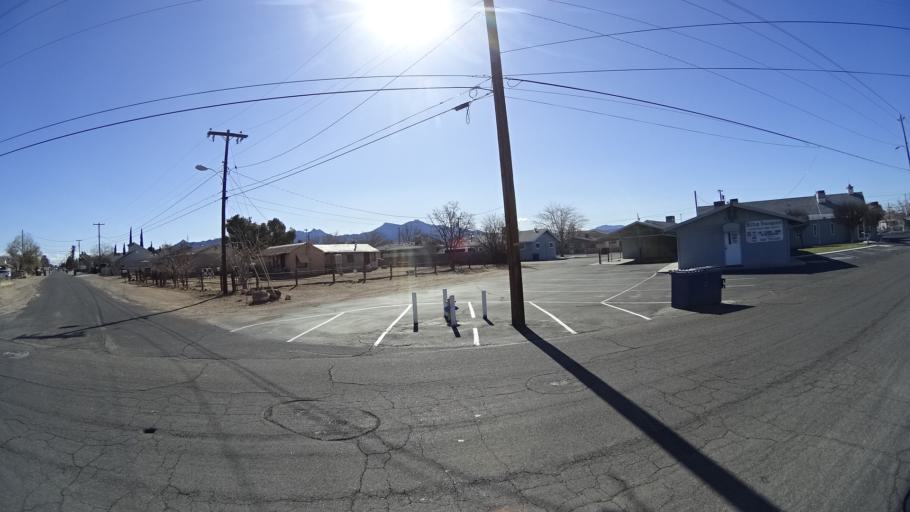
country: US
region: Arizona
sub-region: Mohave County
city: Kingman
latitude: 35.1973
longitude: -114.0253
